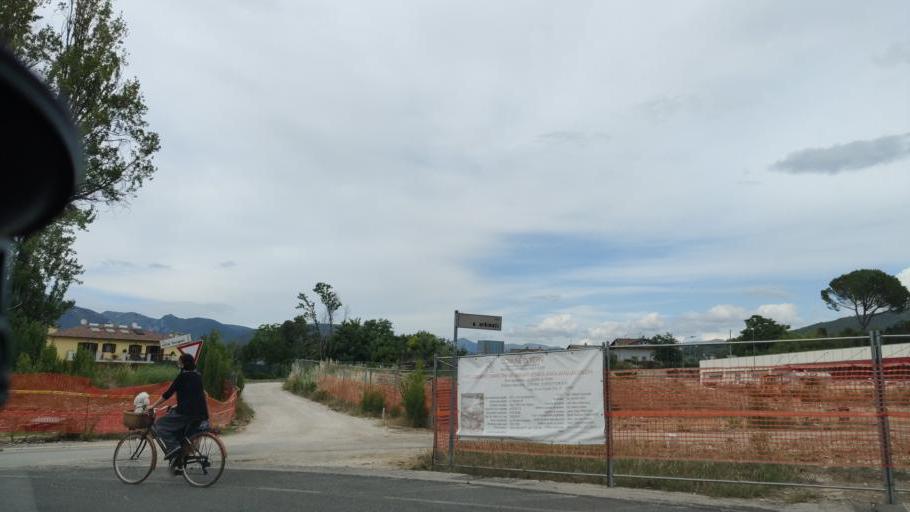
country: IT
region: Umbria
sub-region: Provincia di Terni
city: Terni
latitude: 42.5548
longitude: 12.6589
